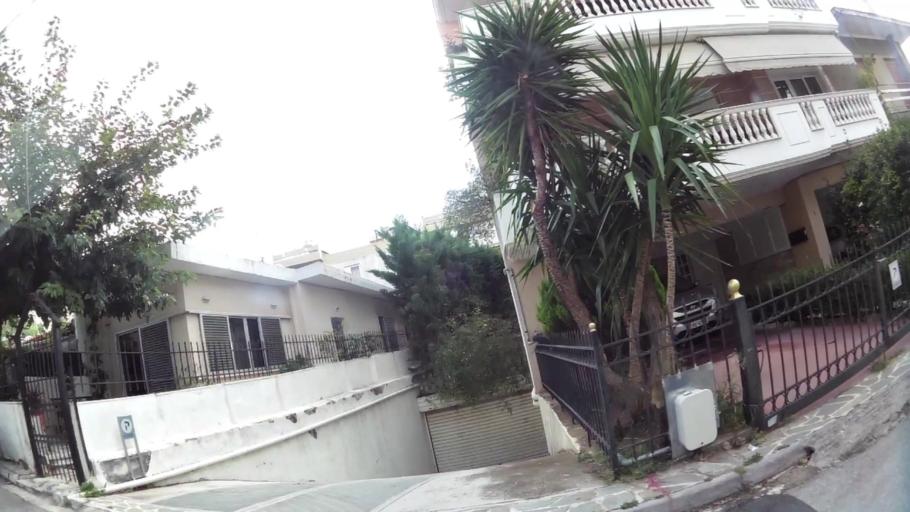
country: GR
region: Attica
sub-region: Nomarchia Athinas
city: Marousi
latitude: 38.0547
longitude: 23.8166
